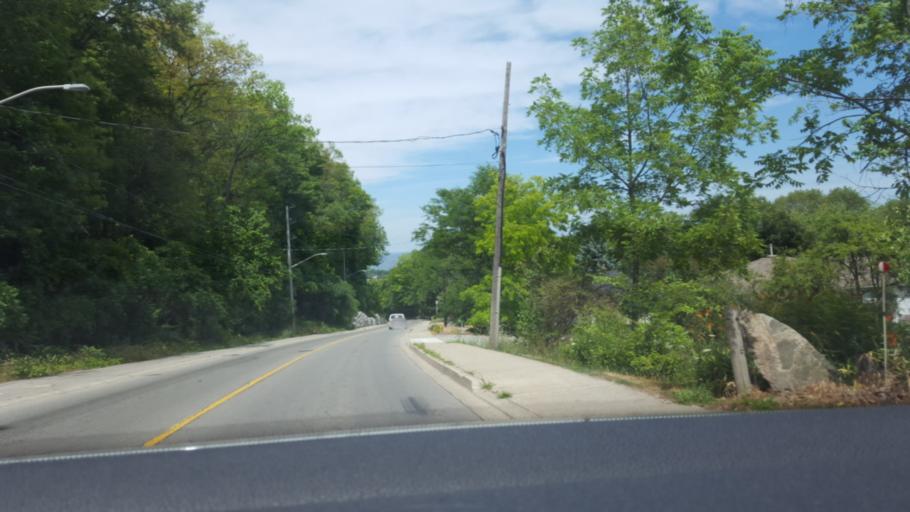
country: CA
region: Ontario
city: Oakville
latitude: 43.1855
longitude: -79.5611
